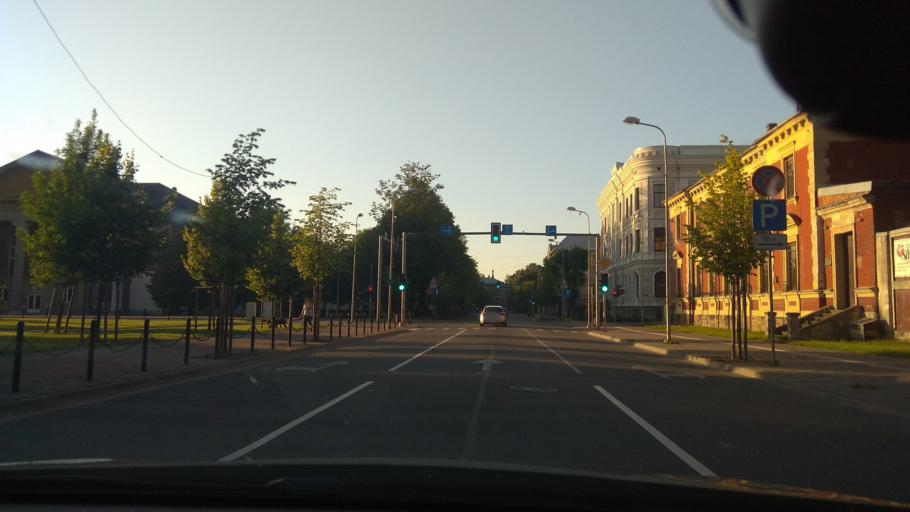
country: LV
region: Jelgava
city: Jelgava
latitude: 56.6433
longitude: 23.7313
